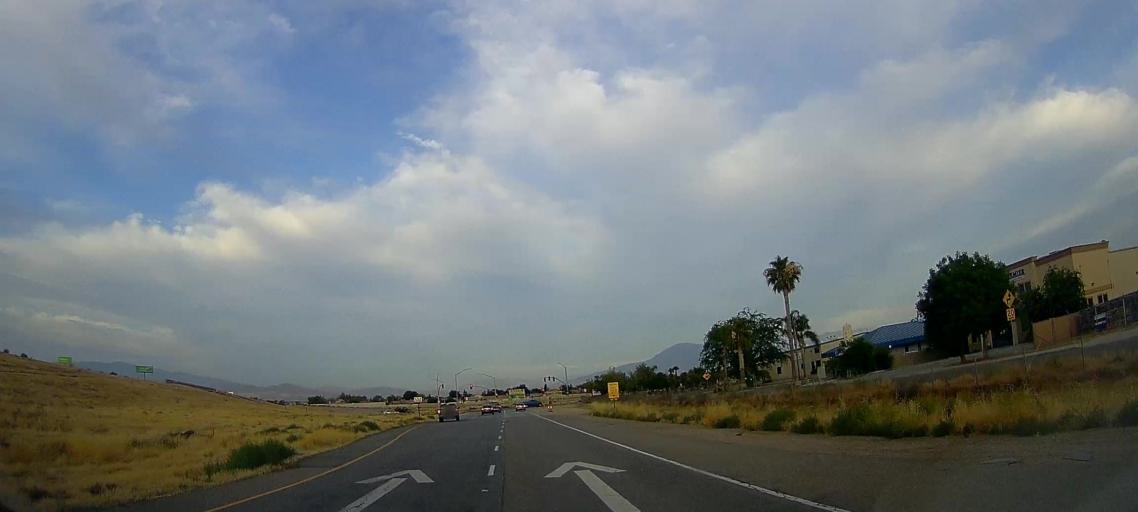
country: US
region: California
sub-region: Kern County
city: Bakersfield
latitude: 35.3517
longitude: -118.9513
